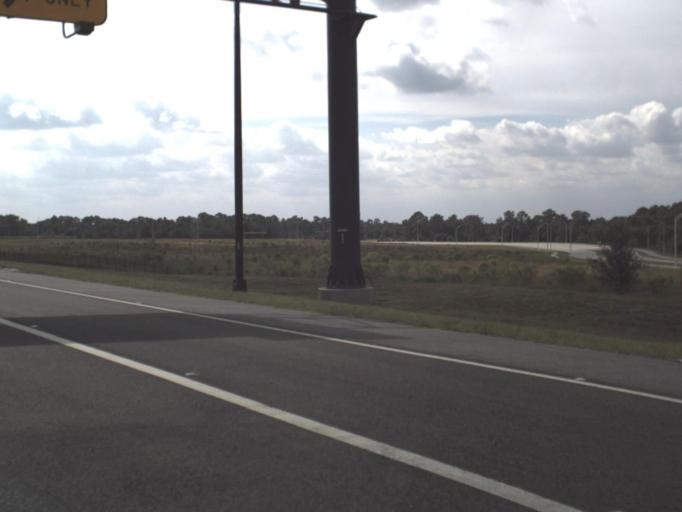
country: US
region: Florida
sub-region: Polk County
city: Polk City
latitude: 28.1408
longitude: -81.8421
